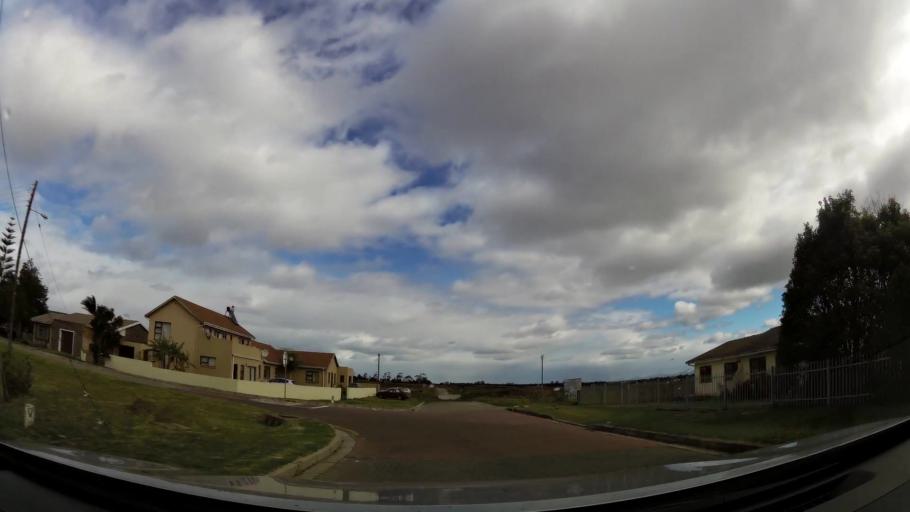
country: ZA
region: Western Cape
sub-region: Eden District Municipality
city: George
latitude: -34.0023
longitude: 22.4430
